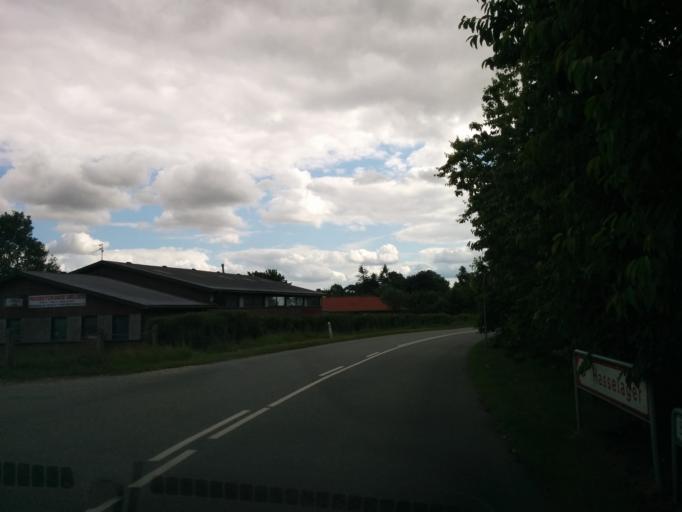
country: DK
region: Central Jutland
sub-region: Arhus Kommune
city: Kolt
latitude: 56.1123
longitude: 10.0709
